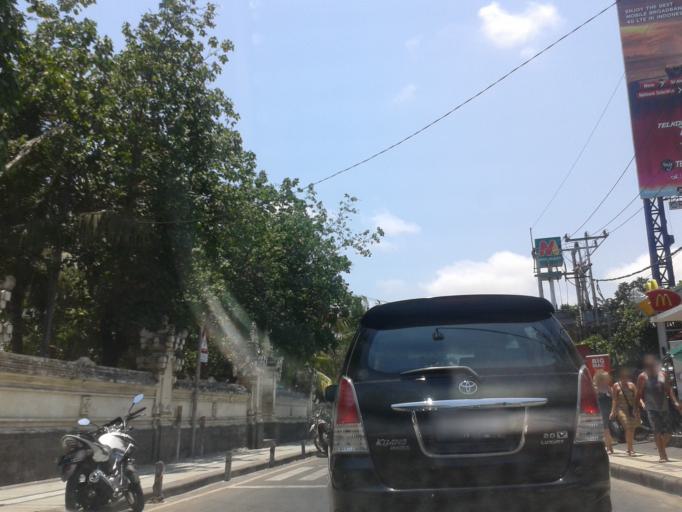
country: ID
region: Bali
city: Kuta
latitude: -8.7200
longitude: 115.1693
